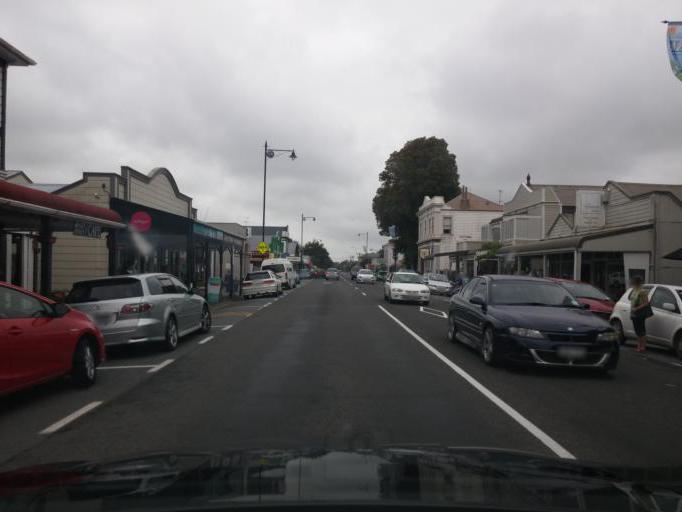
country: NZ
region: Wellington
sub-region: Masterton District
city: Masterton
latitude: -41.0797
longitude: 175.4610
